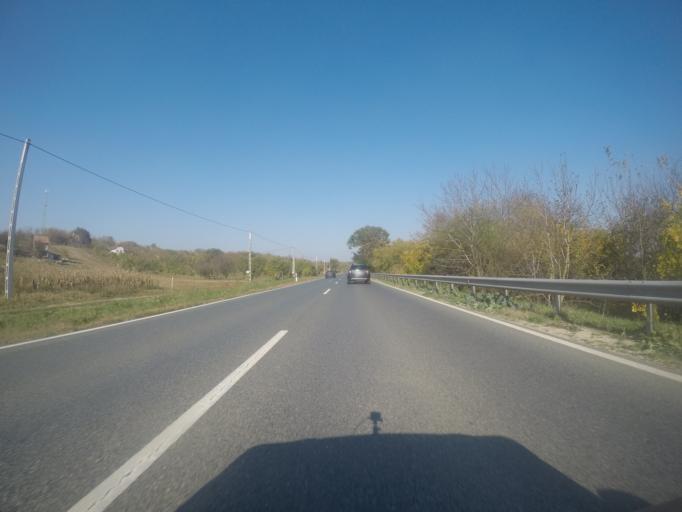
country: HU
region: Tolna
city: Paks
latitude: 46.6807
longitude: 18.8851
